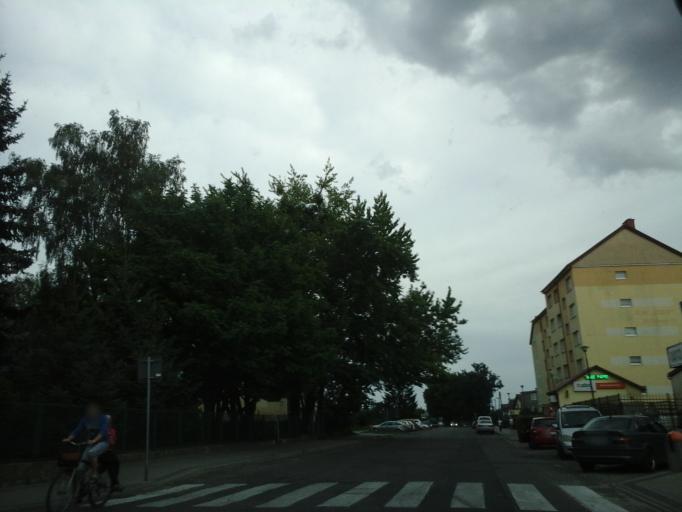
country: PL
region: West Pomeranian Voivodeship
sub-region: Powiat goleniowski
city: Nowogard
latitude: 53.6638
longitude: 15.1253
